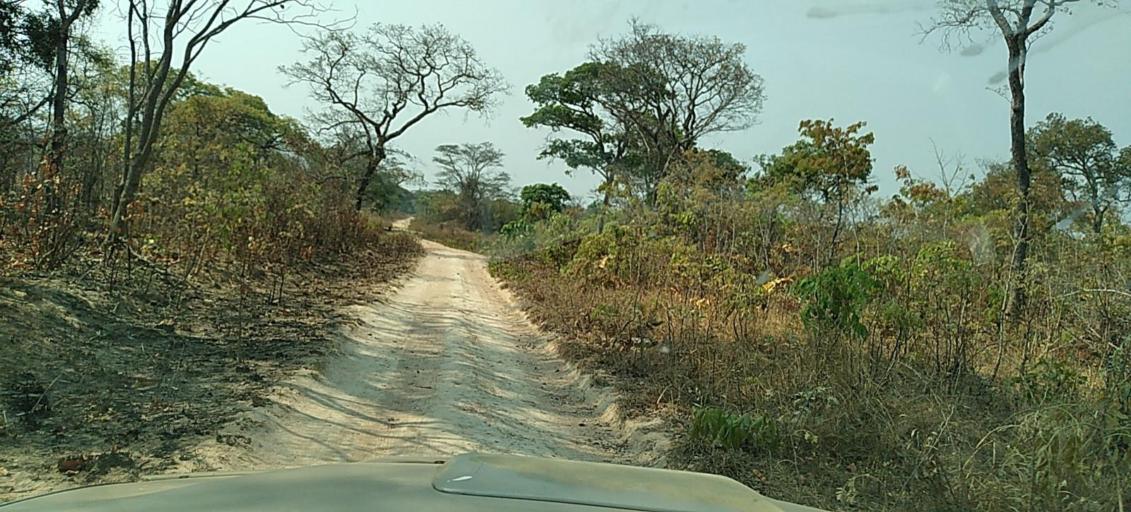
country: ZM
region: North-Western
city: Kasempa
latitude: -13.5417
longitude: 26.4088
